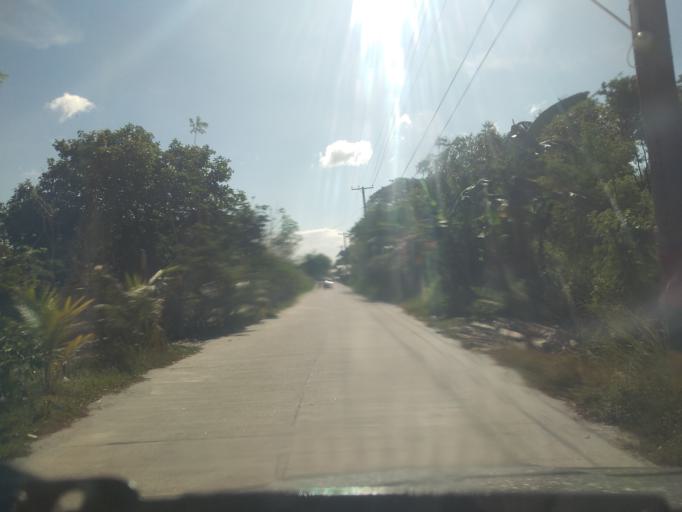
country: PH
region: Central Luzon
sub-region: Province of Pampanga
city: Calibutbut
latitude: 15.0885
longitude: 120.6007
